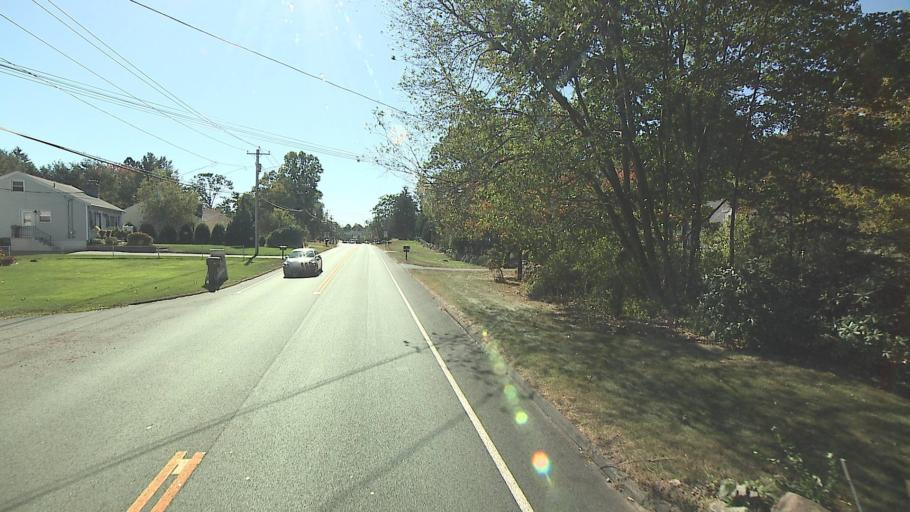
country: US
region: Connecticut
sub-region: New Haven County
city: Orange
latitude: 41.2702
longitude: -73.0017
